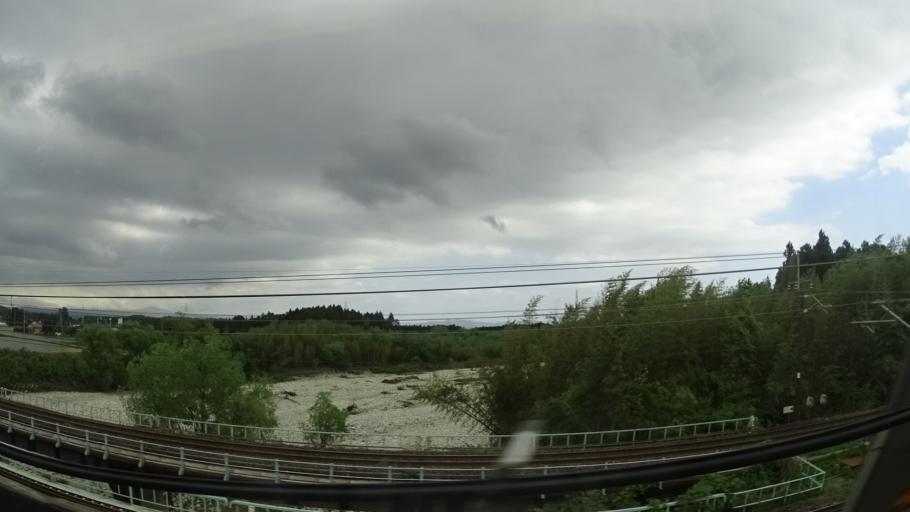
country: JP
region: Tochigi
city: Otawara
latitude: 36.9114
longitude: 140.0058
